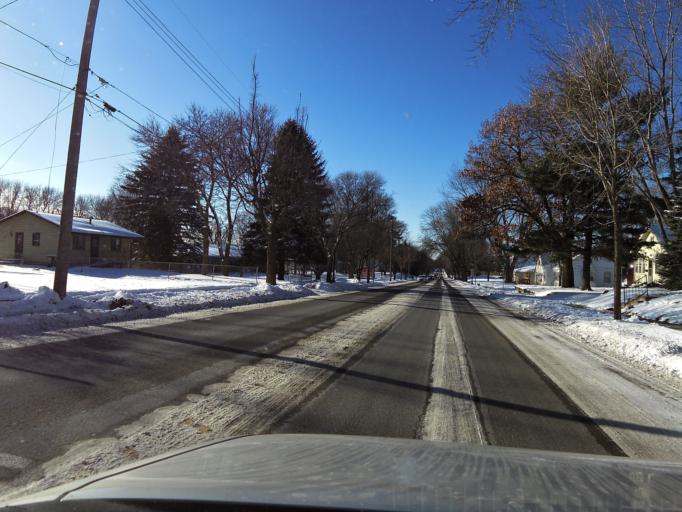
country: US
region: Minnesota
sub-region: Ramsey County
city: Maplewood
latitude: 44.9630
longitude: -93.0068
